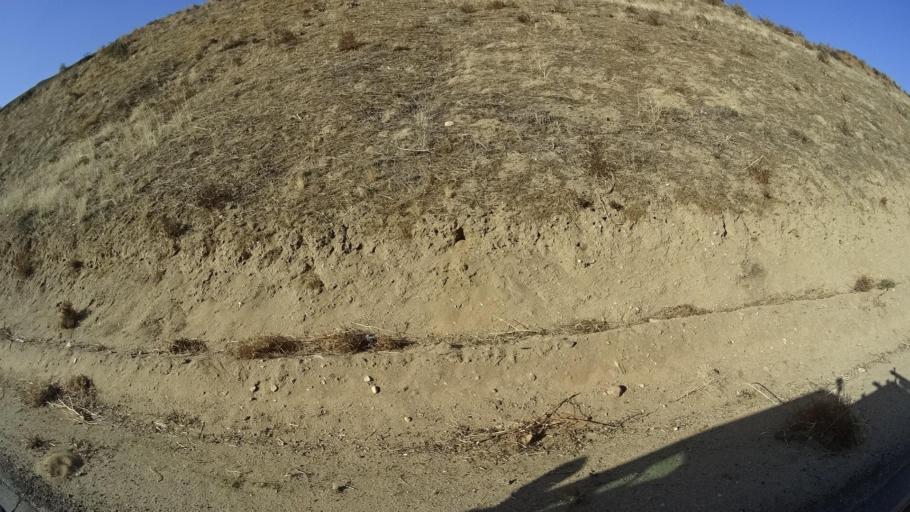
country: US
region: California
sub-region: Kern County
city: Arvin
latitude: 35.3287
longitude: -118.7660
